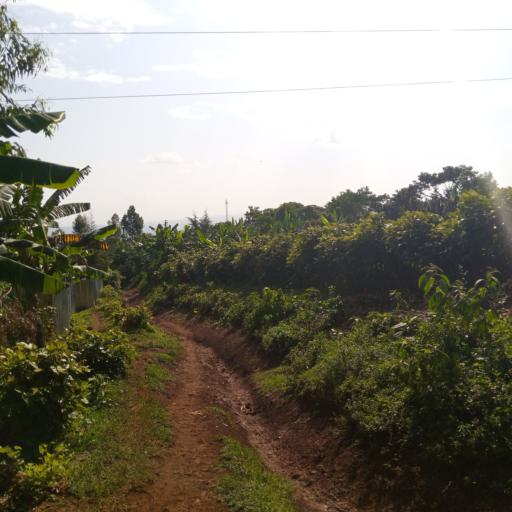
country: ET
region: Oromiya
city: Jima
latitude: 7.6777
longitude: 36.8687
